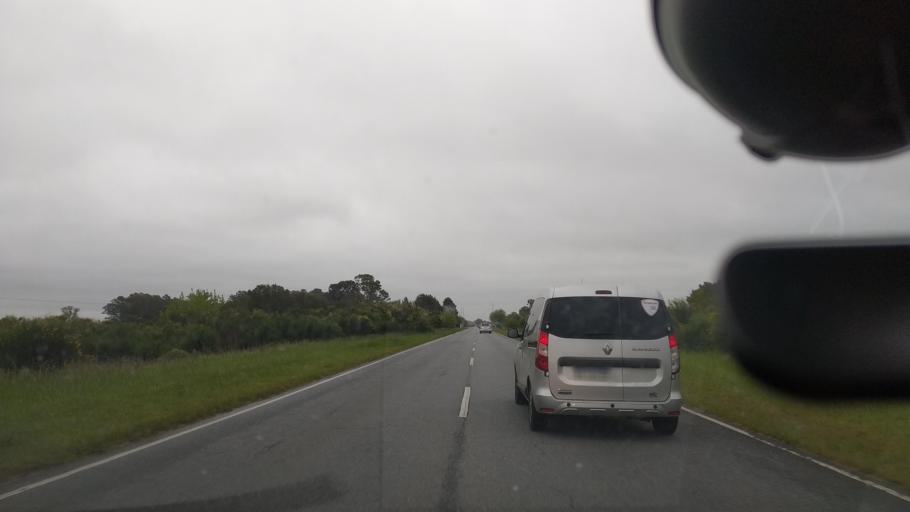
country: AR
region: Buenos Aires
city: Veronica
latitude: -35.4033
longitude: -57.3517
